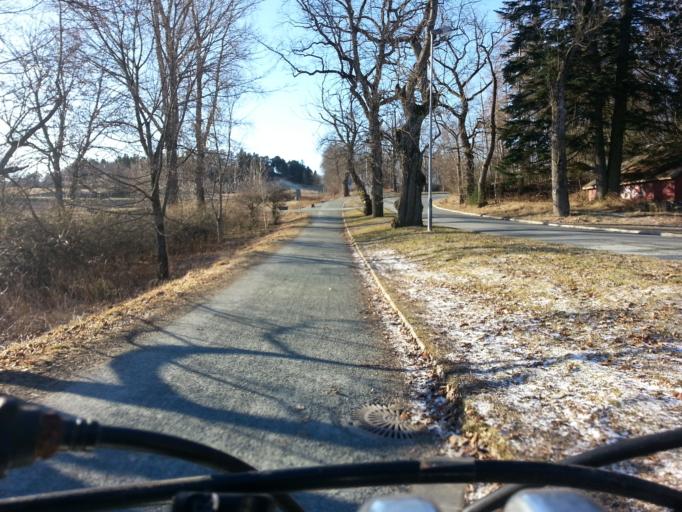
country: NO
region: Sor-Trondelag
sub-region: Trondheim
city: Trondheim
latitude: 63.4379
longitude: 10.4837
